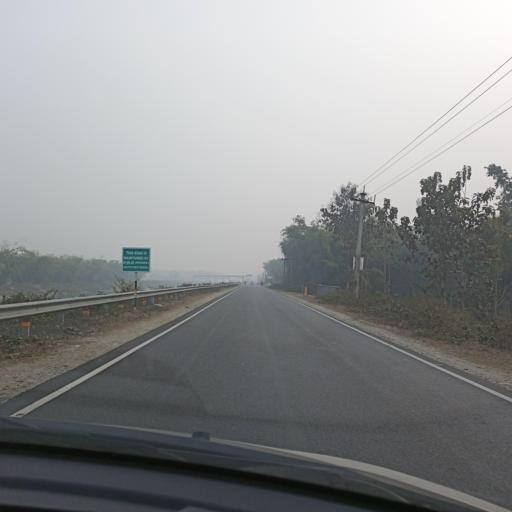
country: IN
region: West Bengal
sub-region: Darjiling
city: Shiliguri
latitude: 26.6807
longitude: 88.5571
